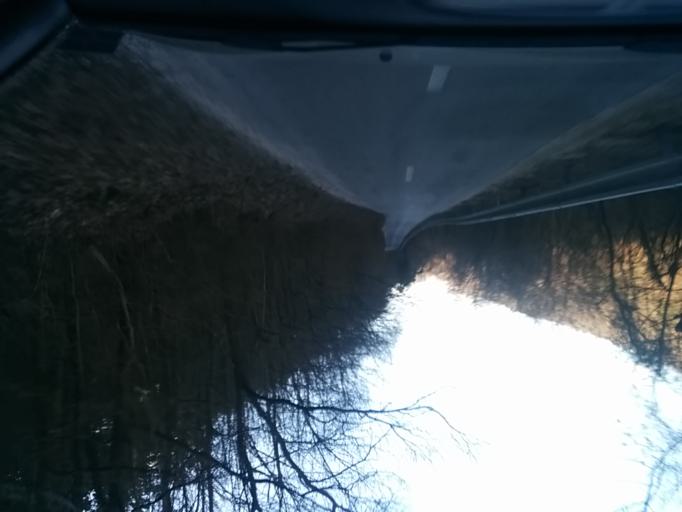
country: SK
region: Nitriansky
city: Cachtice
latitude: 48.7268
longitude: 17.7766
